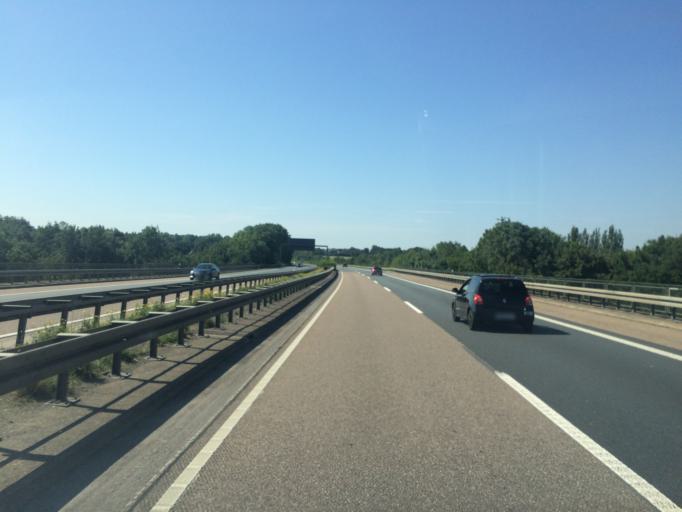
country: DE
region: North Rhine-Westphalia
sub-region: Regierungsbezirk Arnsberg
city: Holzwickede
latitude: 51.5210
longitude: 7.6432
